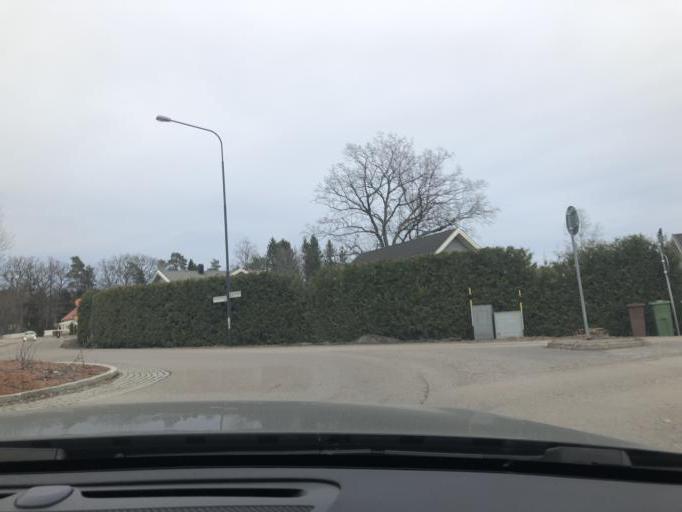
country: SE
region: Stockholm
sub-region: Huddinge Kommun
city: Segeltorp
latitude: 59.2431
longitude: 17.9292
